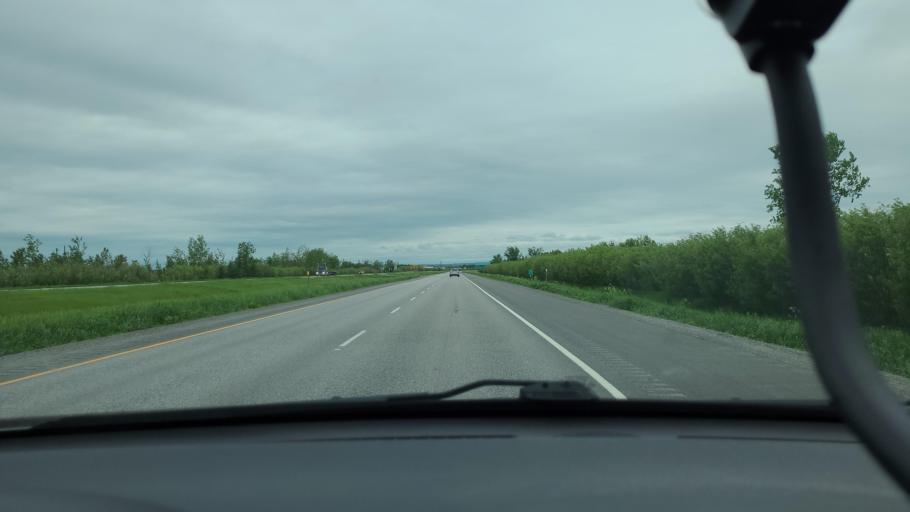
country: CA
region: Quebec
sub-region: Lanaudiere
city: Mascouche
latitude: 45.8475
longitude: -73.6389
